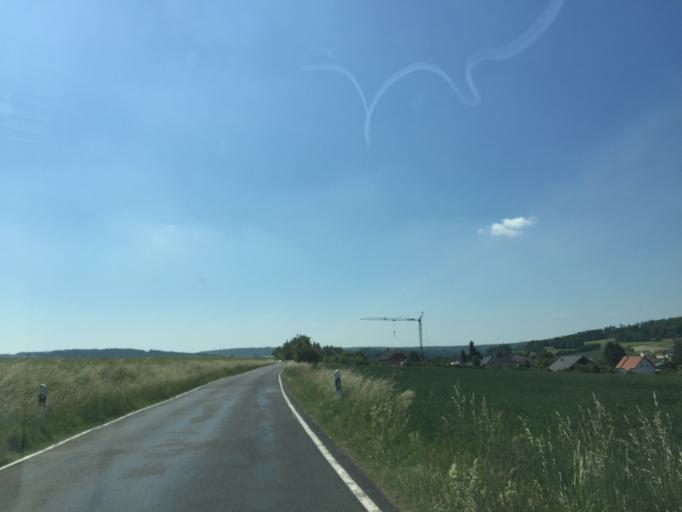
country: DE
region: Bavaria
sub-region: Regierungsbezirk Unterfranken
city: Eichenbuhl
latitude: 49.6416
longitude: 9.3168
